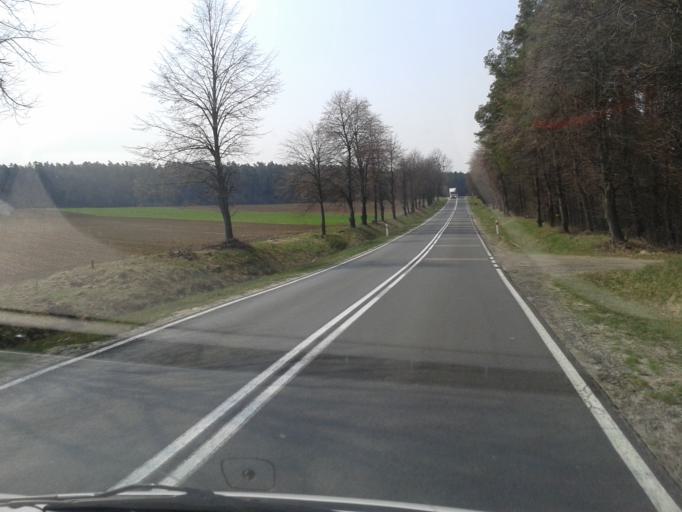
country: PL
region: Subcarpathian Voivodeship
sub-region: Powiat lubaczowski
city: Narol
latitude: 50.3233
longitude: 23.2745
